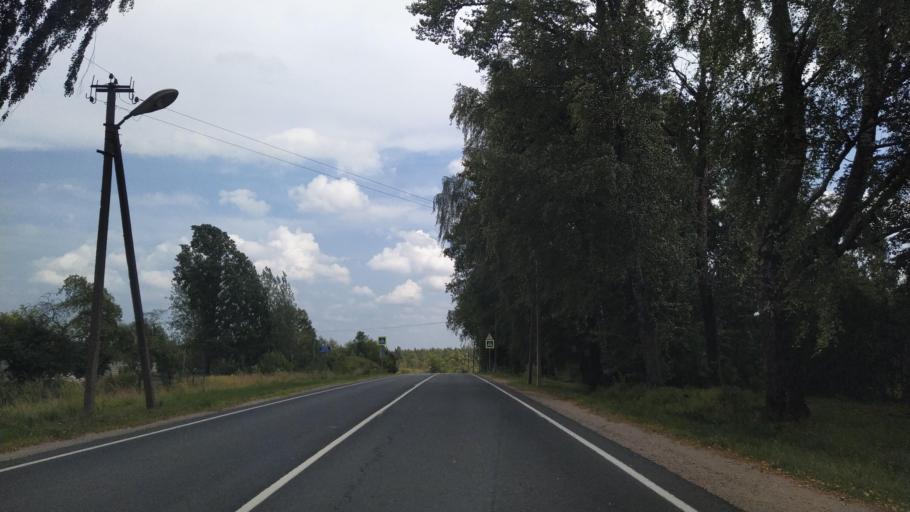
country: RU
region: Pskov
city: Pskov
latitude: 57.7608
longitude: 28.7656
